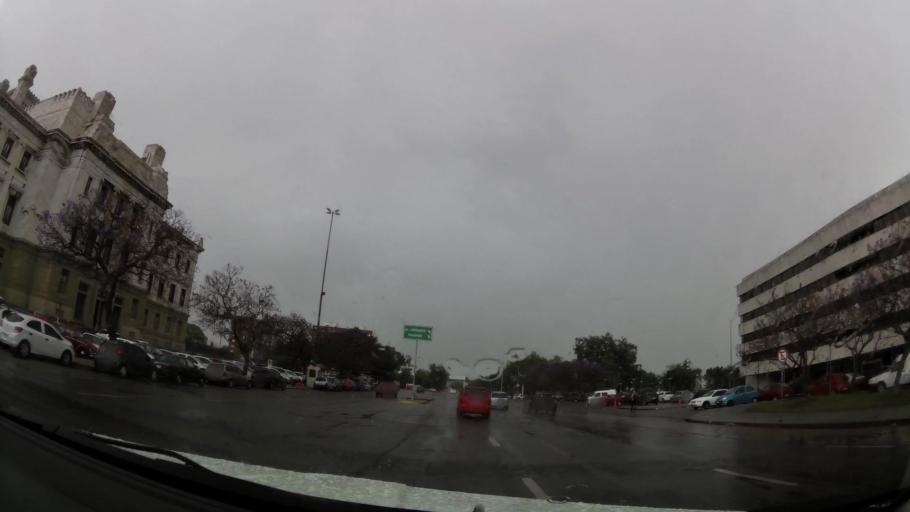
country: UY
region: Montevideo
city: Montevideo
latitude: -34.8906
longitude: -56.1880
